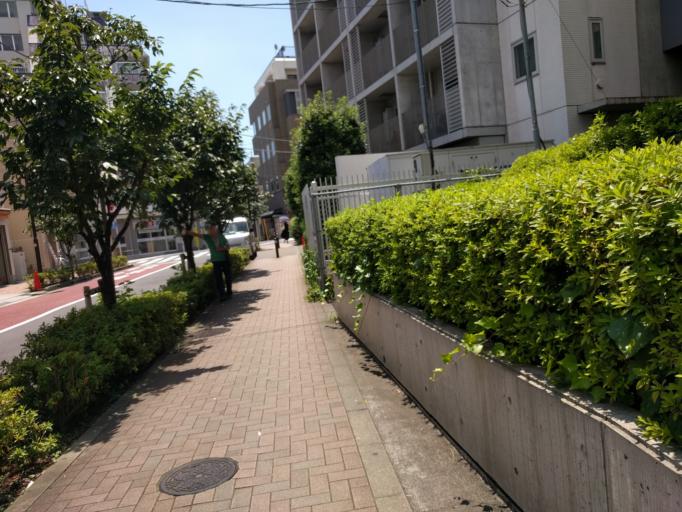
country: JP
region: Tokyo
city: Chofugaoka
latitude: 35.6405
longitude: 139.6003
